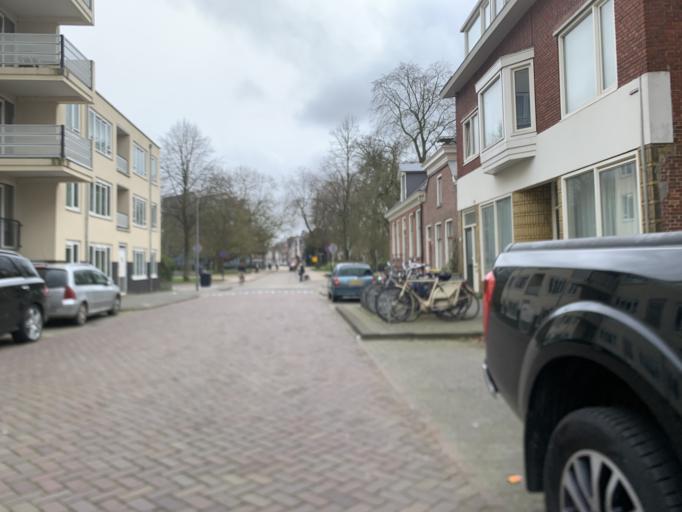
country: NL
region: Groningen
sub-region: Gemeente Groningen
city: Groningen
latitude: 53.2269
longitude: 6.5564
